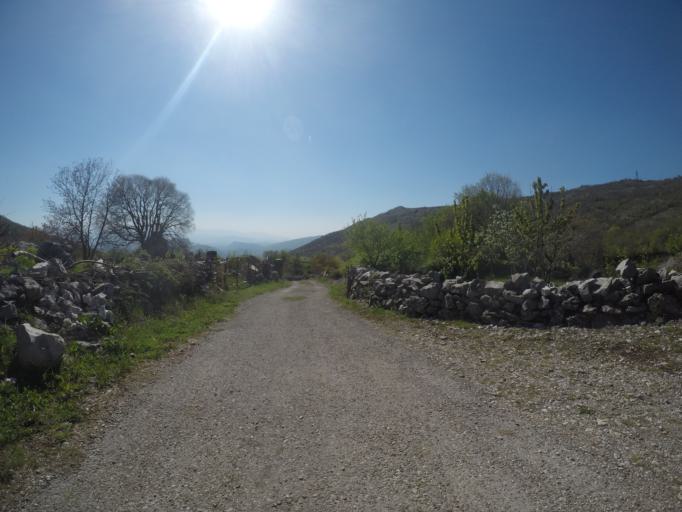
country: ME
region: Danilovgrad
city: Danilovgrad
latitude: 42.5176
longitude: 19.0550
